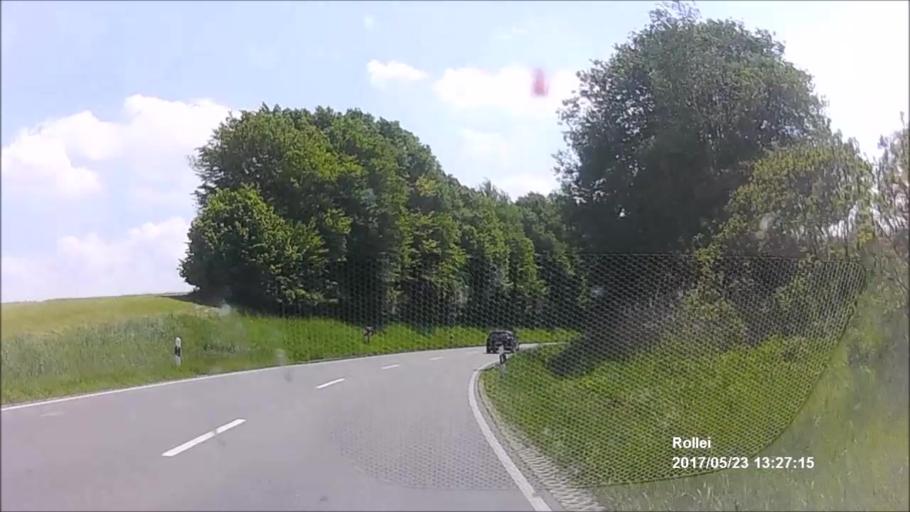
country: DE
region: Bavaria
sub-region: Upper Bavaria
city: Taufkirchen
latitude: 48.3094
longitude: 12.1206
